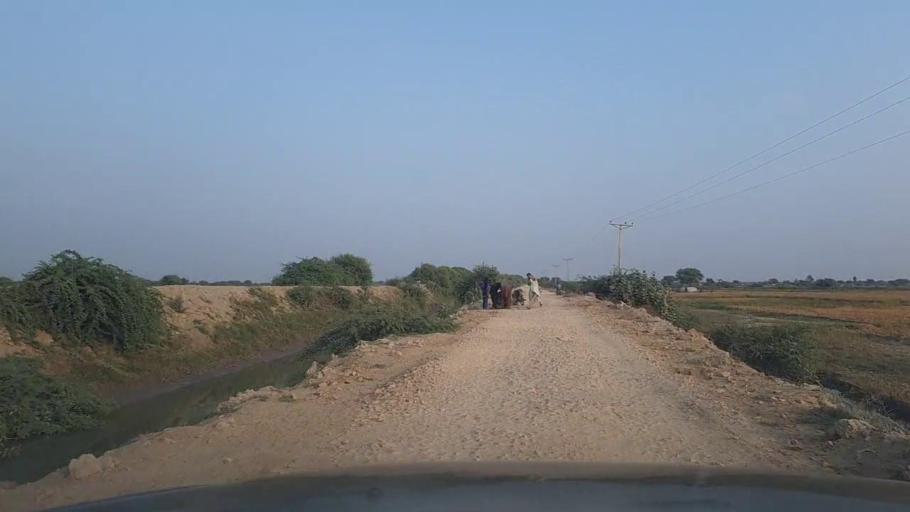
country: PK
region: Sindh
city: Mirpur Batoro
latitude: 24.5456
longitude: 68.3543
